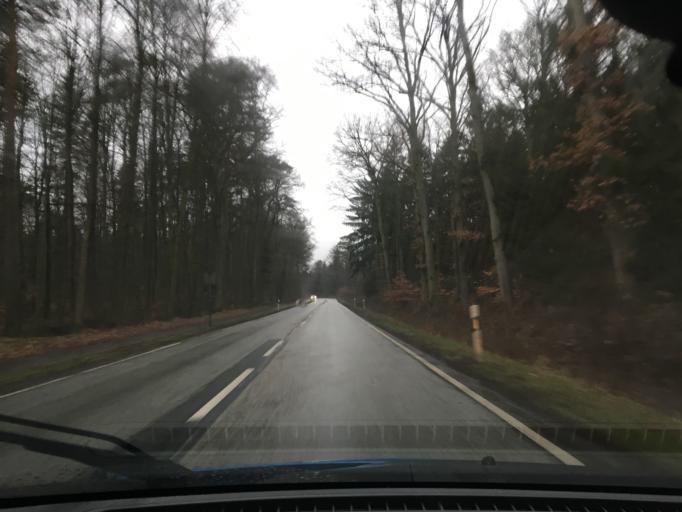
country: DE
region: Schleswig-Holstein
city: Krukow
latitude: 53.3967
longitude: 10.4677
